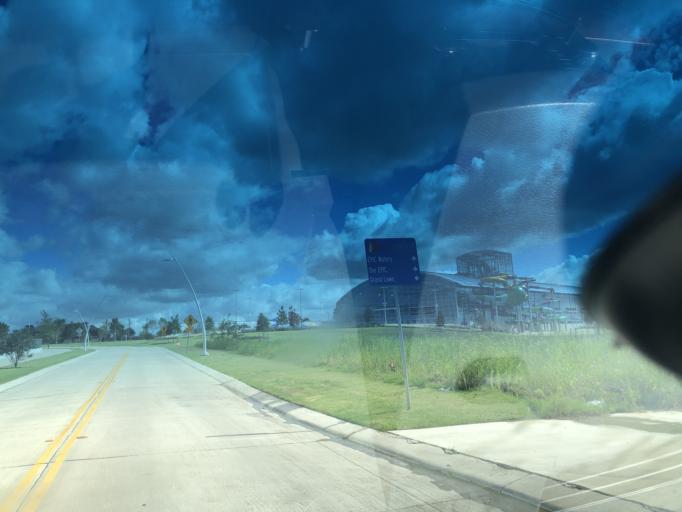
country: US
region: Texas
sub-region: Dallas County
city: Grand Prairie
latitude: 32.7004
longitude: -97.0329
